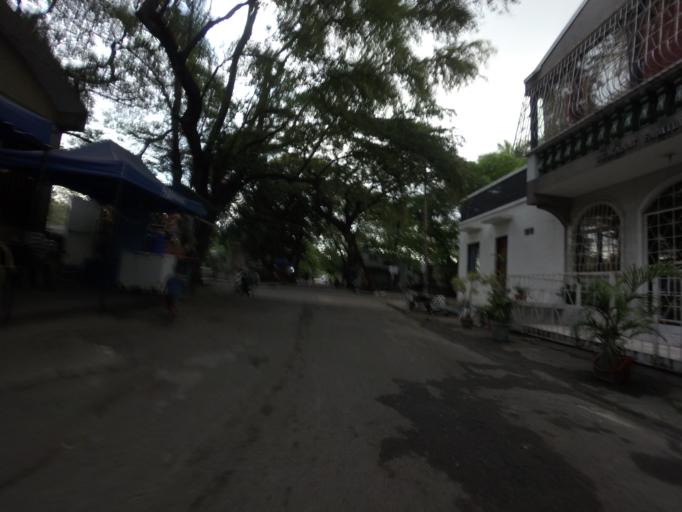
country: PH
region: Metro Manila
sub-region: Makati City
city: Makati City
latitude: 14.5659
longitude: 121.0184
